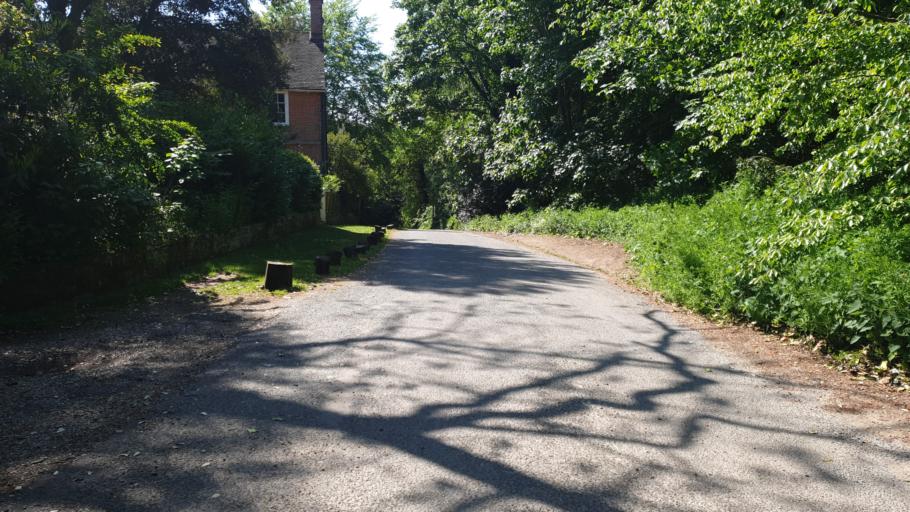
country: GB
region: England
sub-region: Essex
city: Manningtree
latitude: 51.9426
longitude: 1.0373
